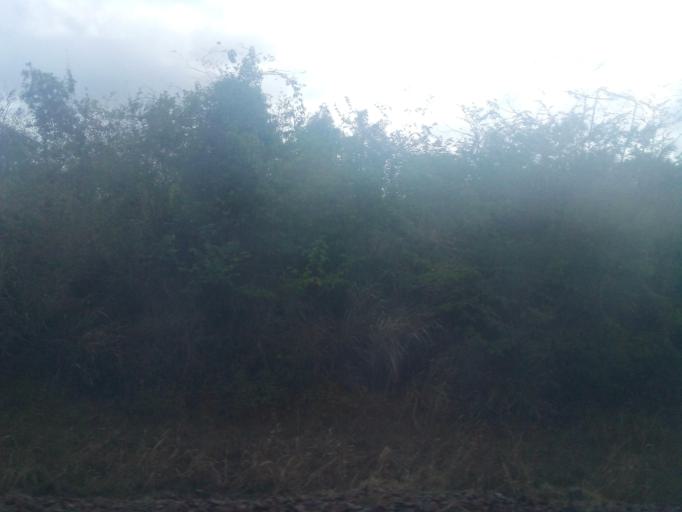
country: BR
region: Maranhao
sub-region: Sao Luis
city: Sao Luis
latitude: -2.6419
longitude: -44.3054
